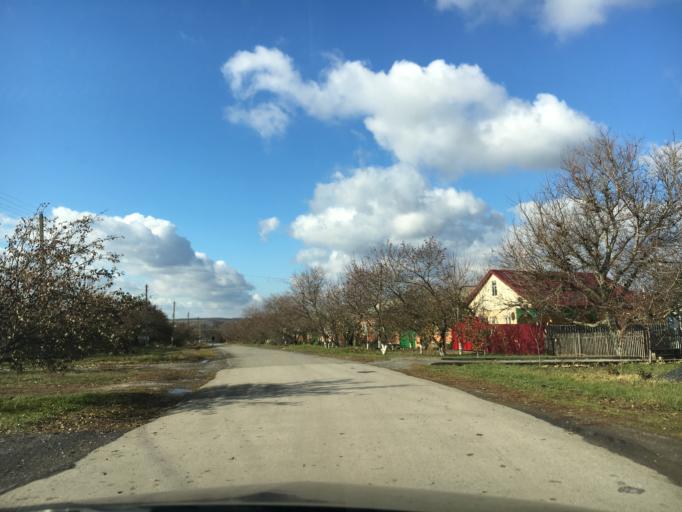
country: RU
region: Rostov
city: Pokrovskoye
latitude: 47.4809
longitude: 38.9179
